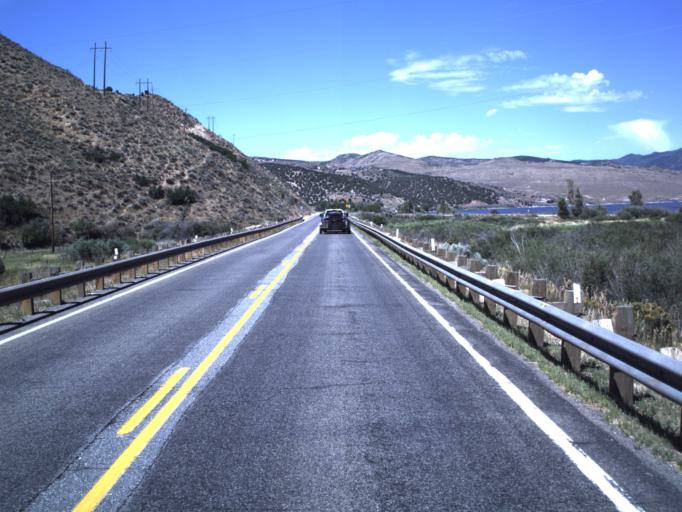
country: US
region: Utah
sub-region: Summit County
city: Oakley
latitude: 40.7517
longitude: -111.3728
